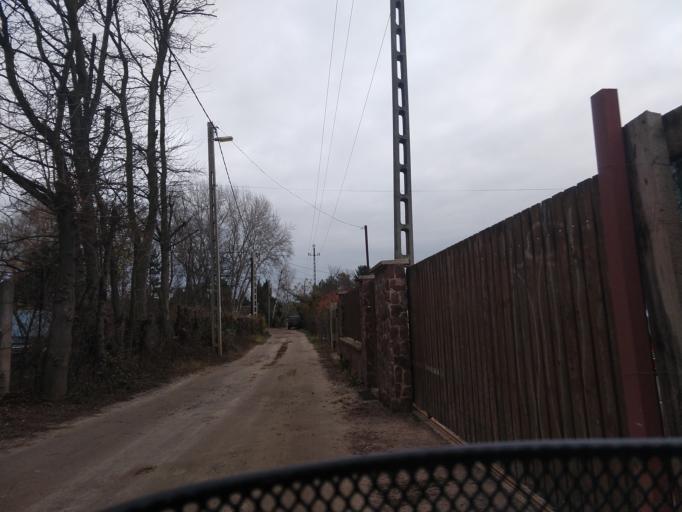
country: HU
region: Pest
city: Orbottyan
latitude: 47.6774
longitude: 19.2879
